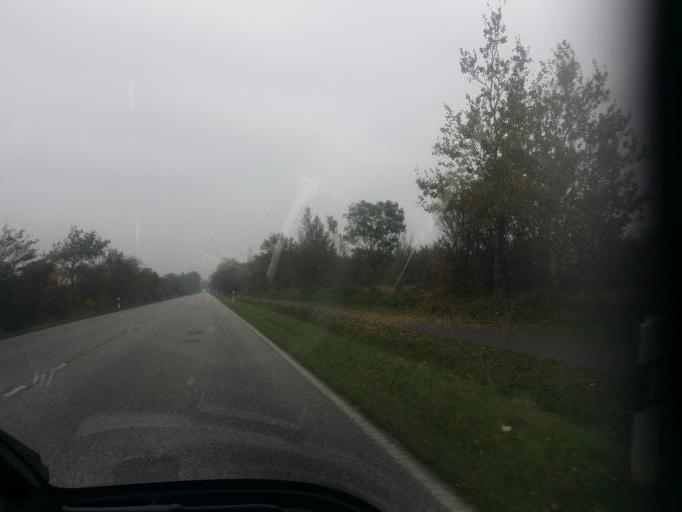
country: DE
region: Schleswig-Holstein
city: Hattstedt
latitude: 54.5138
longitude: 9.0355
